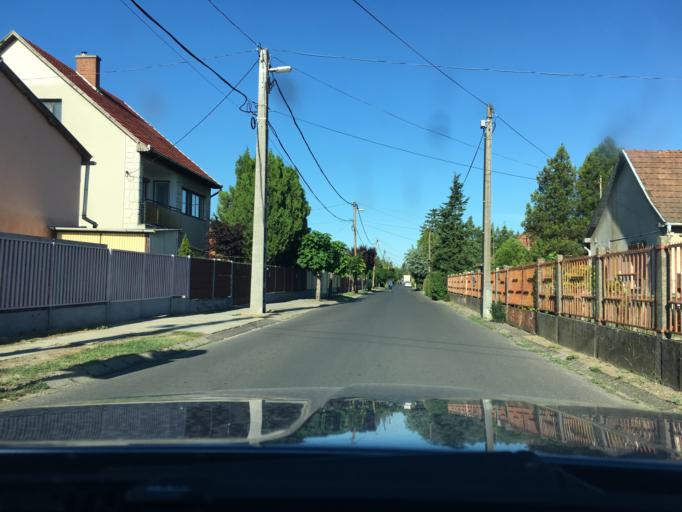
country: HU
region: Hajdu-Bihar
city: Debrecen
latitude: 47.5391
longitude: 21.6596
